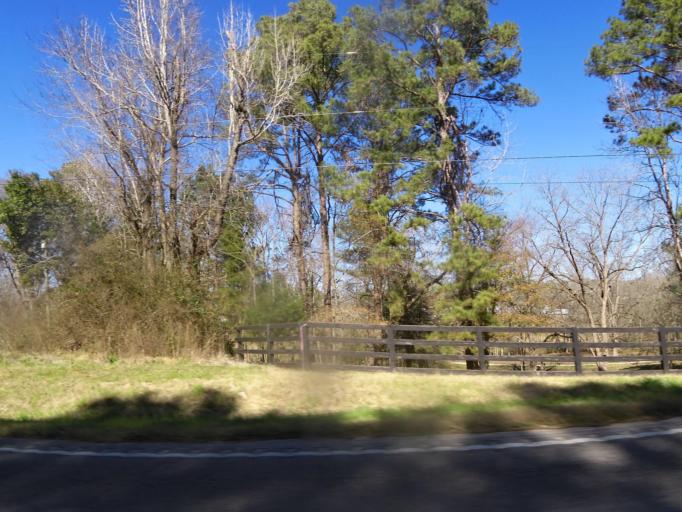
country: US
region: Alabama
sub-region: Bullock County
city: Union Springs
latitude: 32.1371
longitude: -85.7371
